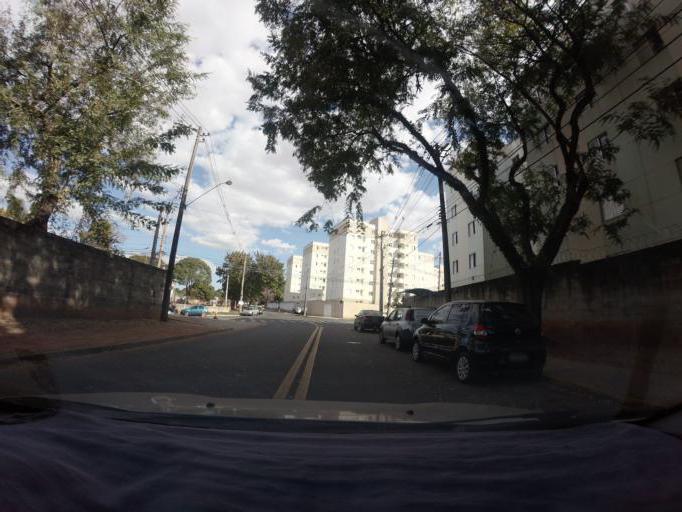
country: BR
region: Sao Paulo
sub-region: Piracicaba
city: Piracicaba
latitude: -22.7406
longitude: -47.5910
